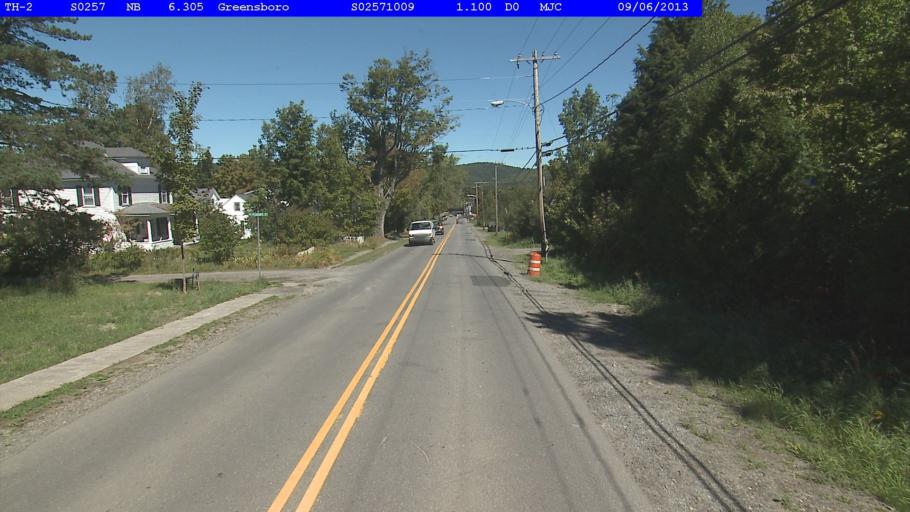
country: US
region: Vermont
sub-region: Caledonia County
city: Hardwick
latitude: 44.5726
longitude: -72.2980
